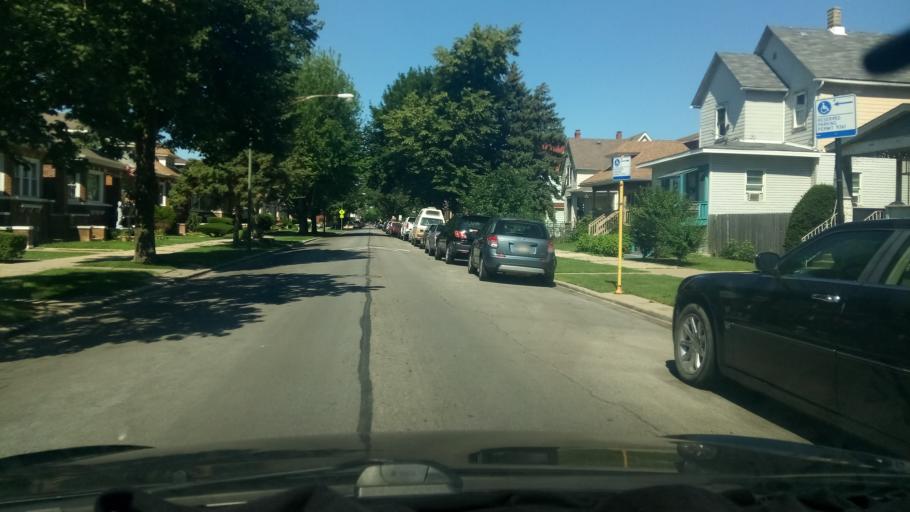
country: US
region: Illinois
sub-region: Cook County
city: Hometown
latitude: 41.7807
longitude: -87.7135
